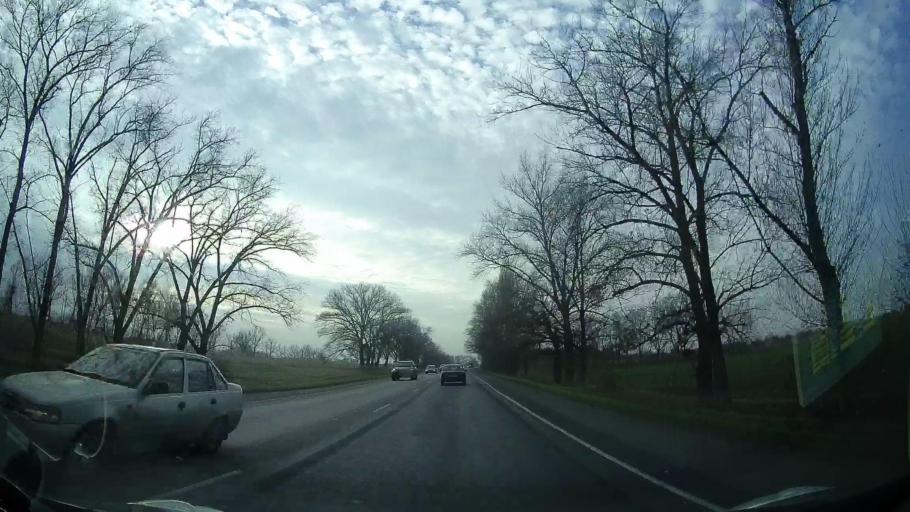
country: RU
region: Rostov
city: Bagayevskaya
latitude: 47.1618
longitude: 40.2465
